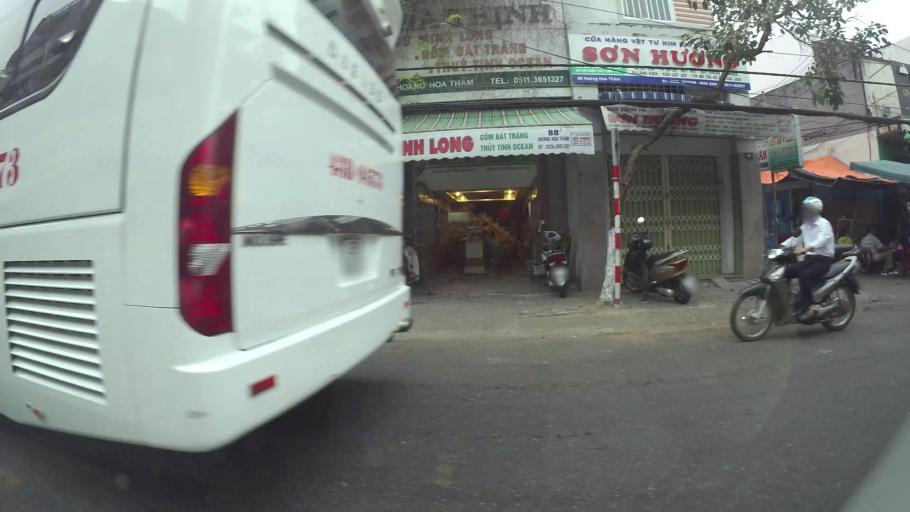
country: VN
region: Da Nang
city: Da Nang
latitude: 16.0679
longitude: 108.2100
